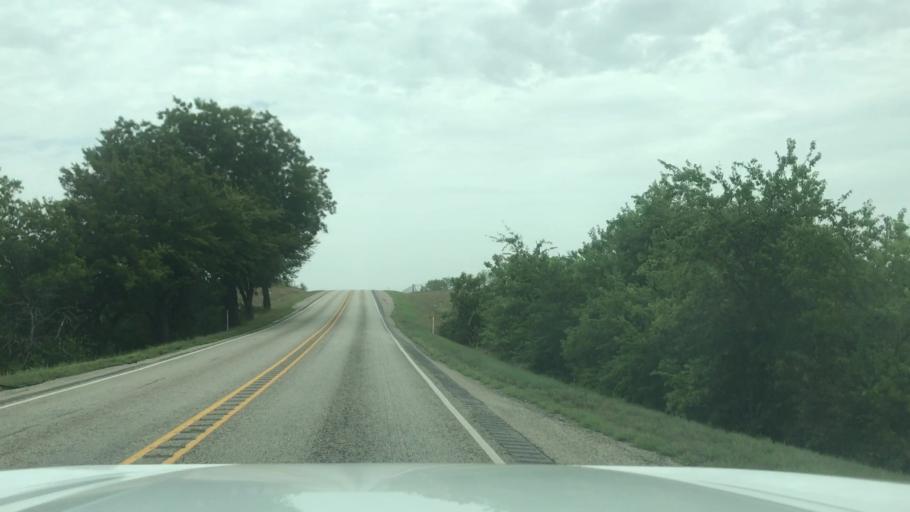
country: US
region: Texas
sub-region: Hamilton County
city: Hico
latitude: 32.0543
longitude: -98.1759
